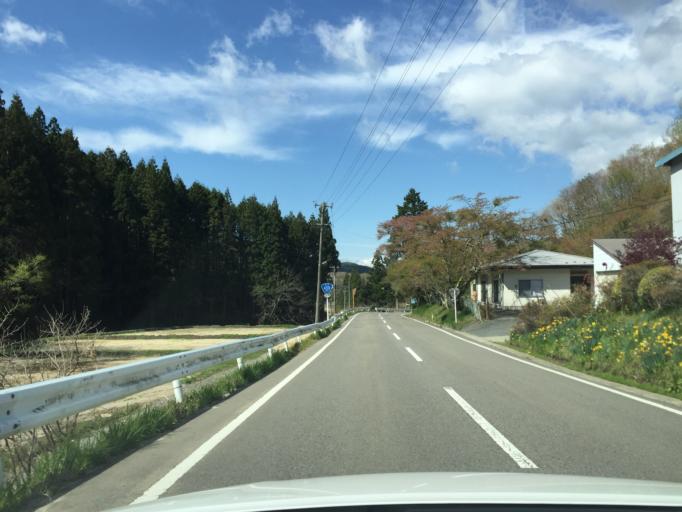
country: JP
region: Fukushima
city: Funehikimachi-funehiki
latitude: 37.5648
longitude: 140.6916
